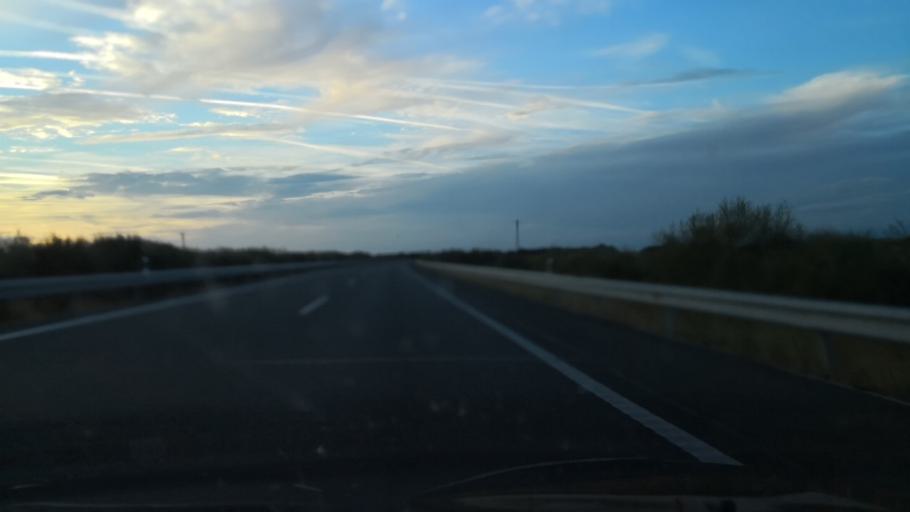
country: ES
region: Extremadura
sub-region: Provincia de Caceres
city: Aldea del Cano
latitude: 39.2643
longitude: -6.3174
